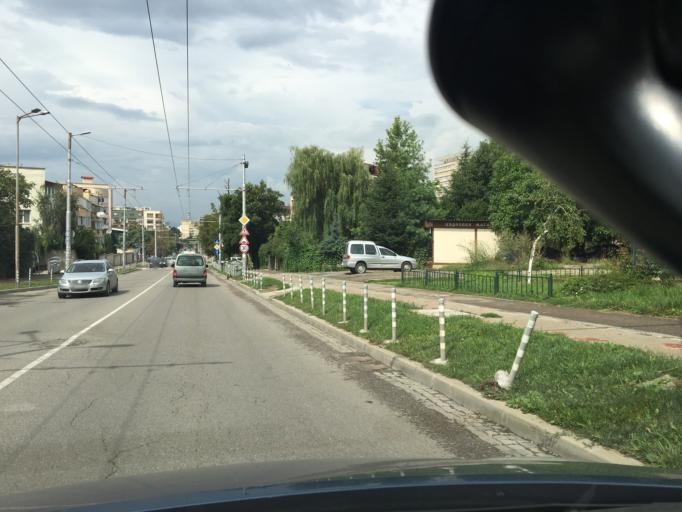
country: BG
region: Sofia-Capital
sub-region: Stolichna Obshtina
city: Sofia
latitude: 42.6606
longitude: 23.2732
